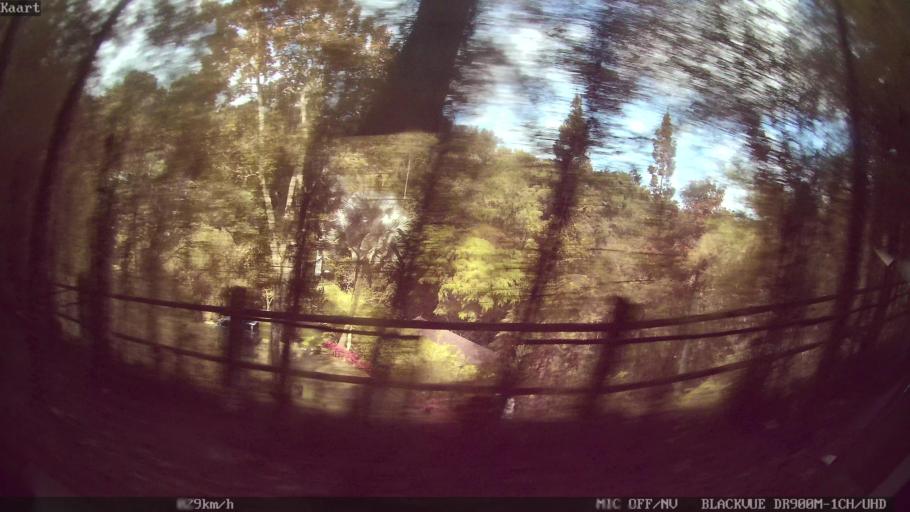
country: ID
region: Bali
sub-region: Kabupaten Gianyar
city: Ubud
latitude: -8.5086
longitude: 115.2786
